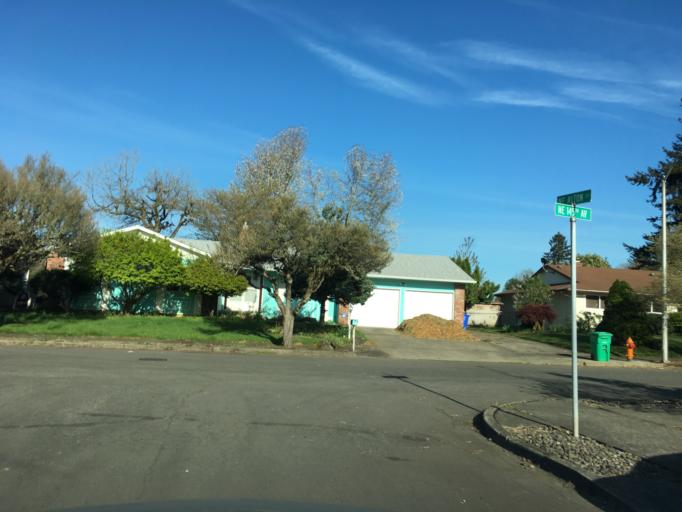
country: US
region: Oregon
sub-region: Multnomah County
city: Fairview
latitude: 45.5497
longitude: -122.5136
